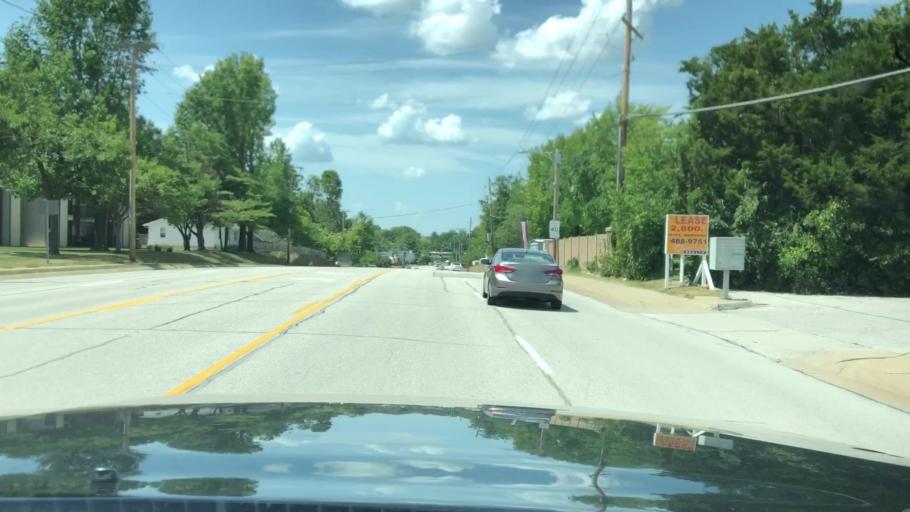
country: US
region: Missouri
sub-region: Saint Charles County
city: Saint Peters
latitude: 38.7895
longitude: -90.6085
